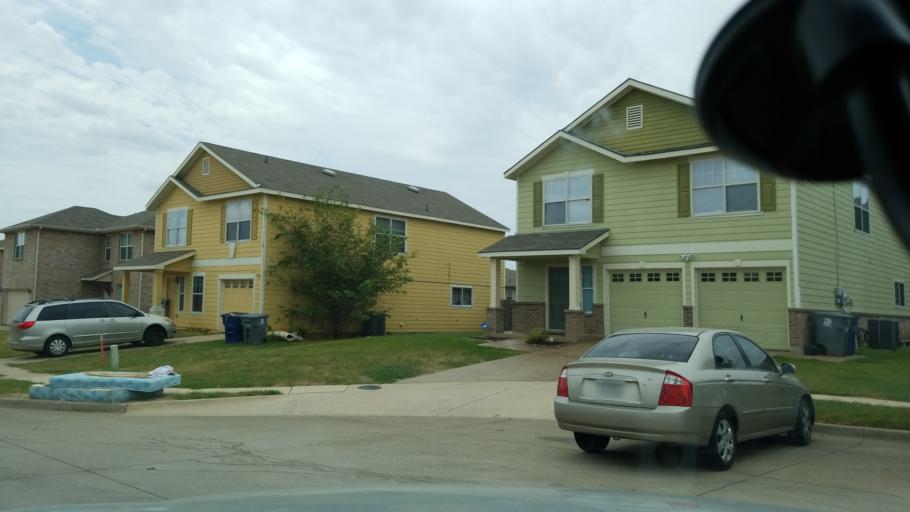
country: US
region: Texas
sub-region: Dallas County
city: Grand Prairie
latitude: 32.7344
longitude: -96.9918
